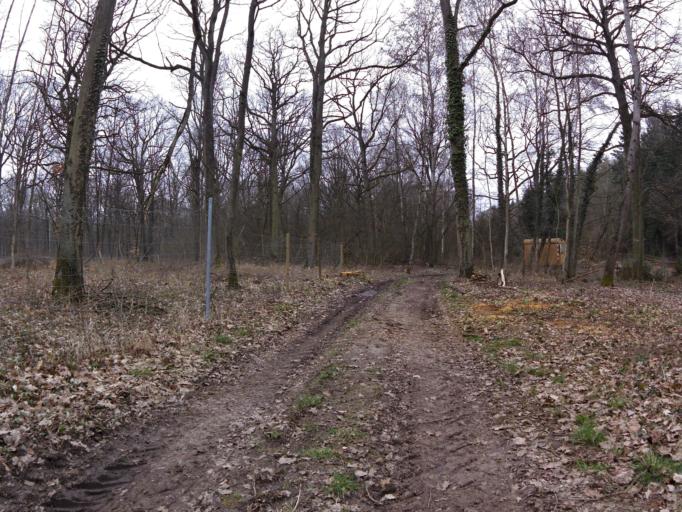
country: DE
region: Bavaria
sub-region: Regierungsbezirk Unterfranken
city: Rottendorf
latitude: 49.8124
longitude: 10.0371
